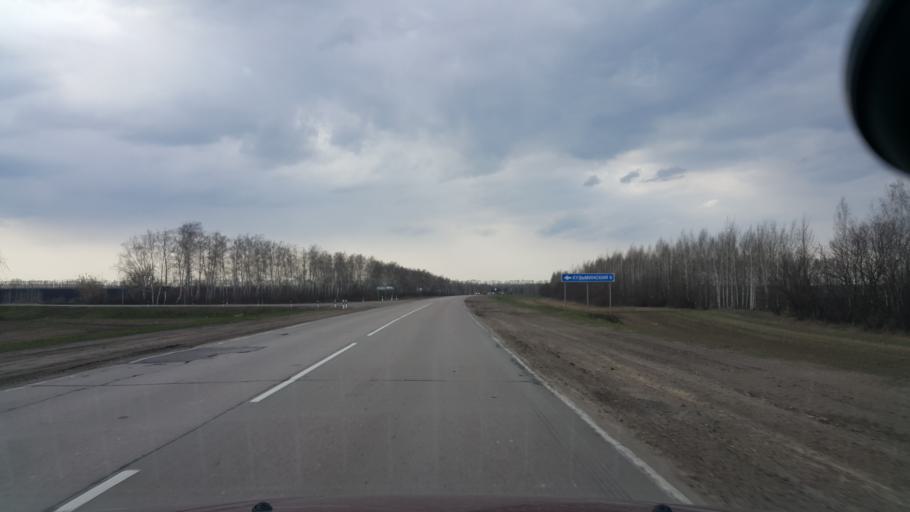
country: RU
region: Tambov
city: Znamenka
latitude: 52.4114
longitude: 41.3811
